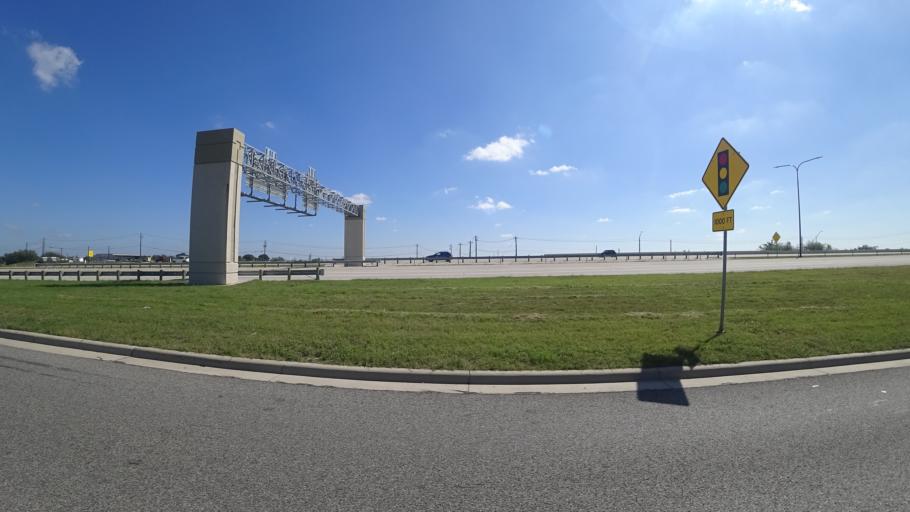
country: US
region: Texas
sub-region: Travis County
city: Manor
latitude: 30.3359
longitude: -97.6046
